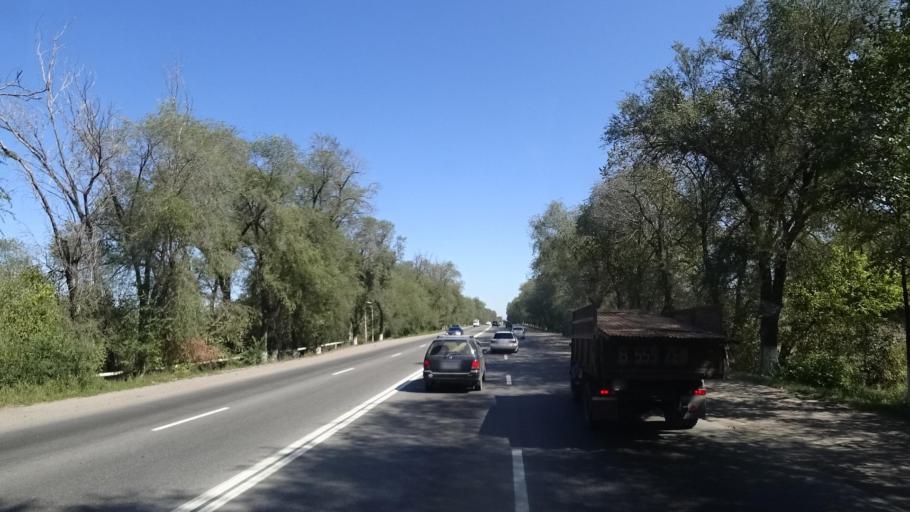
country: KZ
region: Almaty Oblysy
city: Energeticheskiy
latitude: 43.3749
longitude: 77.0992
